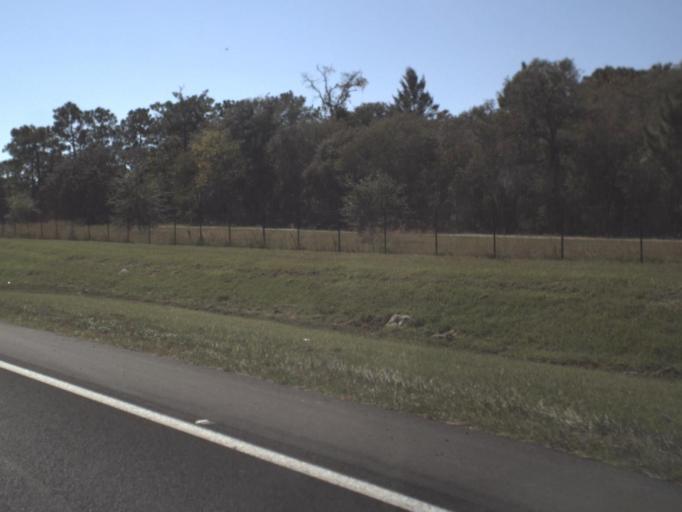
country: US
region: Florida
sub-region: Hernando County
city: Masaryktown
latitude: 28.4760
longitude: -82.4800
